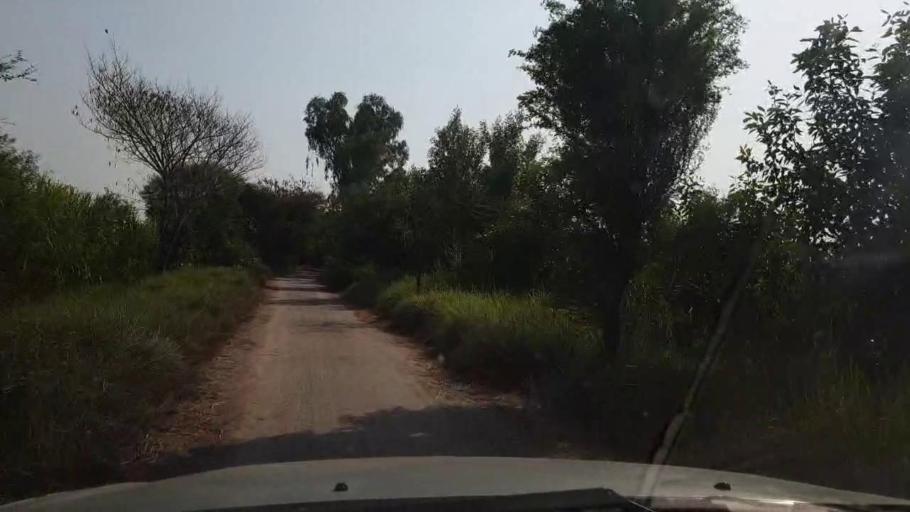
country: PK
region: Sindh
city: Bulri
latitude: 24.8993
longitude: 68.3762
